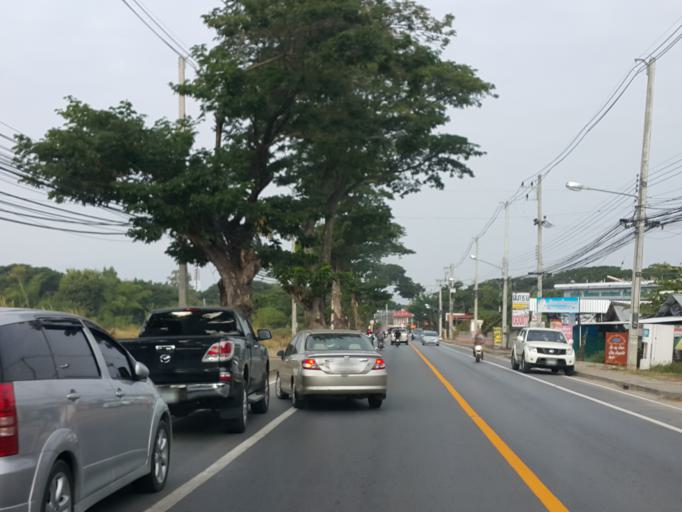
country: TH
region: Chiang Mai
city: Saraphi
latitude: 18.7757
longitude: 99.0593
